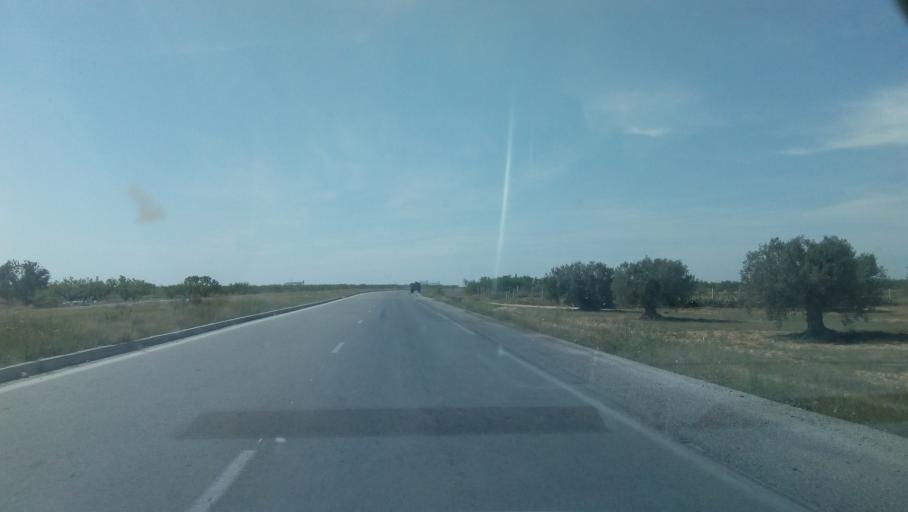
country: TN
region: Safaqis
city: Al Qarmadah
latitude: 34.8605
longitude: 10.7926
